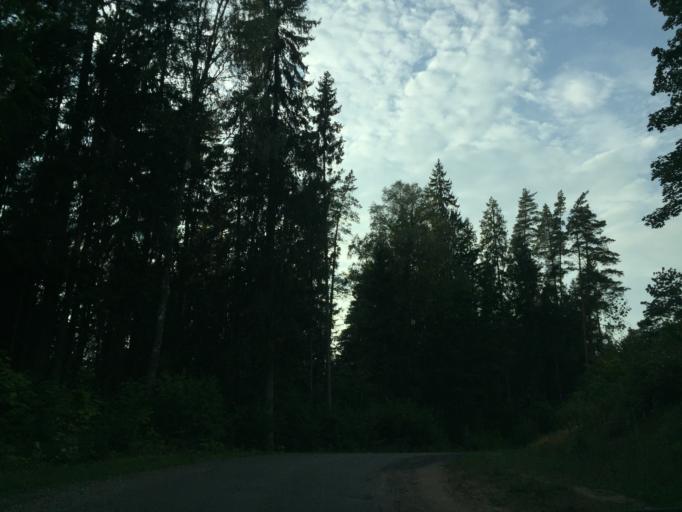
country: LV
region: Baldone
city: Baldone
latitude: 56.7729
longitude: 24.4165
